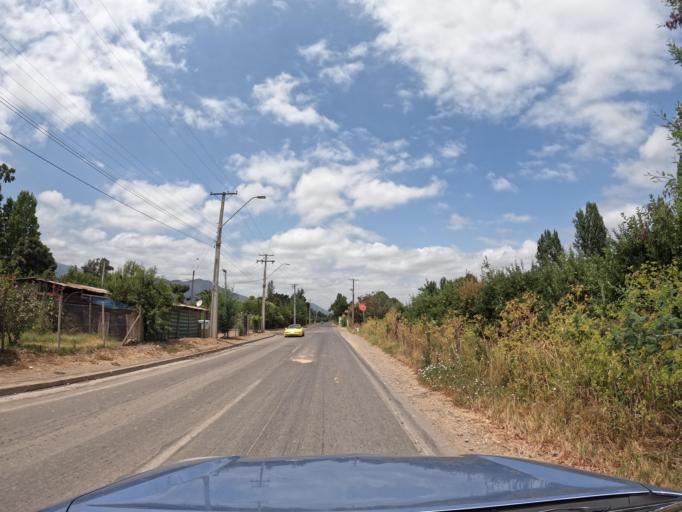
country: CL
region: O'Higgins
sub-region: Provincia de Colchagua
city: Chimbarongo
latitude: -34.7529
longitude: -70.9537
